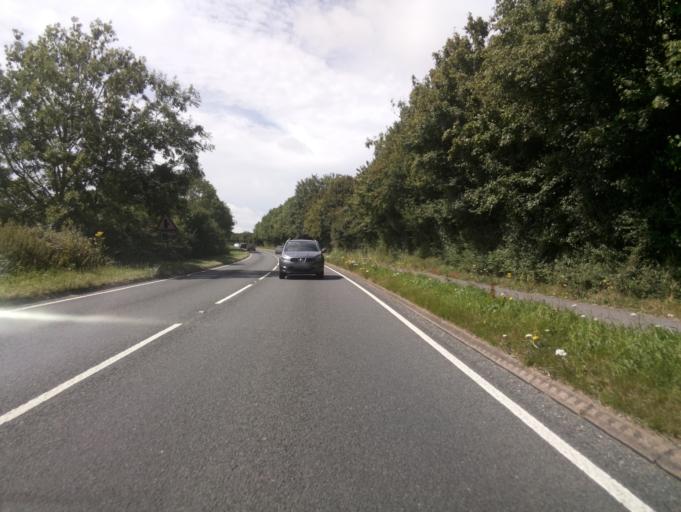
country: GB
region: England
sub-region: Dorset
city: Dorchester
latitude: 50.7325
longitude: -2.4624
